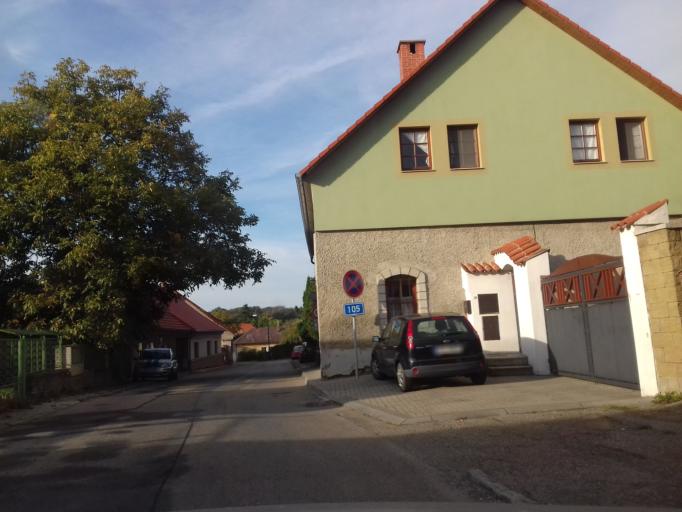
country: CZ
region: Central Bohemia
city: Neveklov
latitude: 49.7534
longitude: 14.5304
